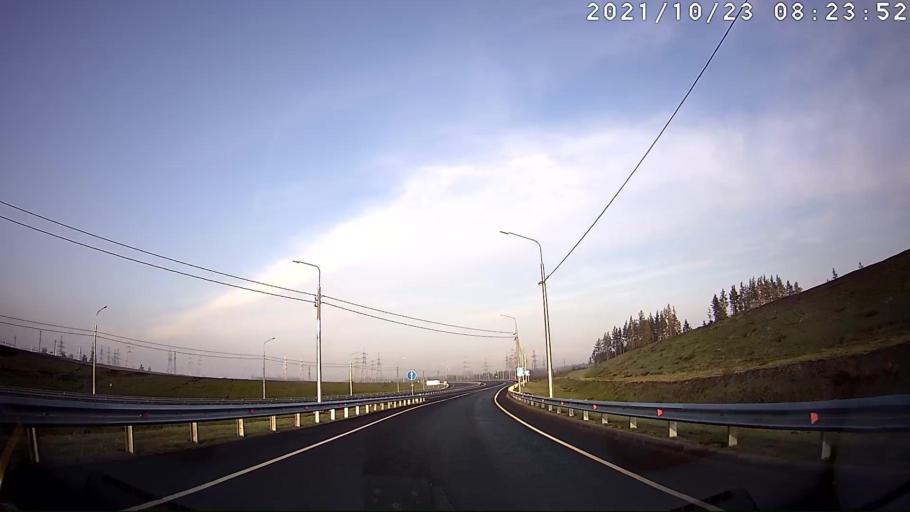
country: RU
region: Saratov
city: Sennoy
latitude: 52.1429
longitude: 46.9162
